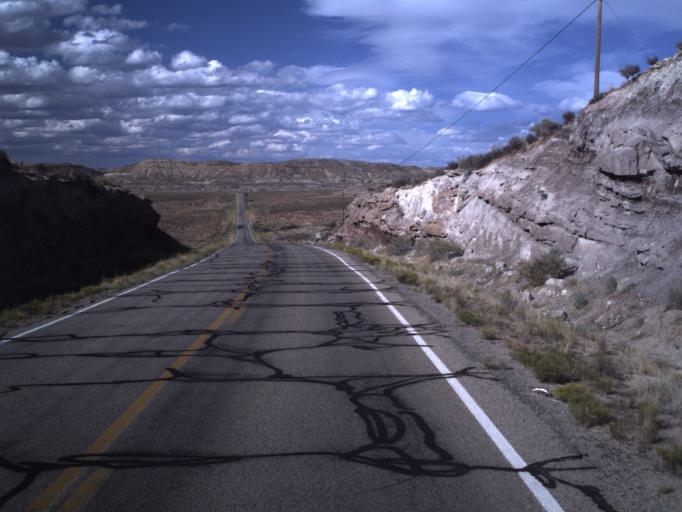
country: US
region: Utah
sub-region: San Juan County
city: Blanding
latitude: 37.2875
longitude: -109.2900
